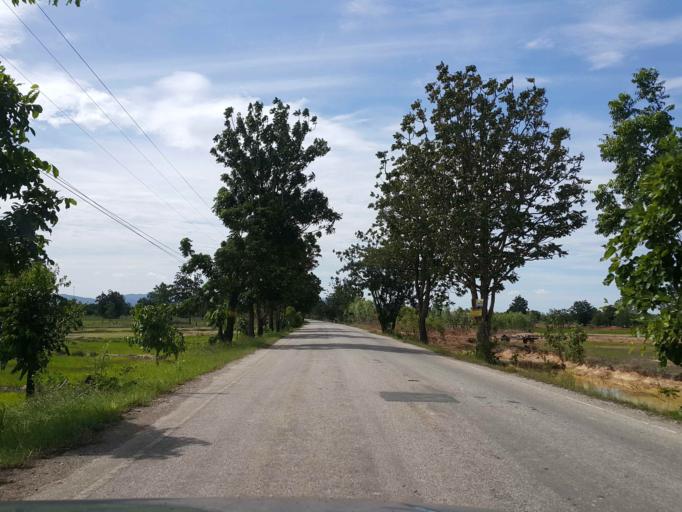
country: TH
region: Sukhothai
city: Ban Dan Lan Hoi
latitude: 17.1315
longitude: 99.5278
